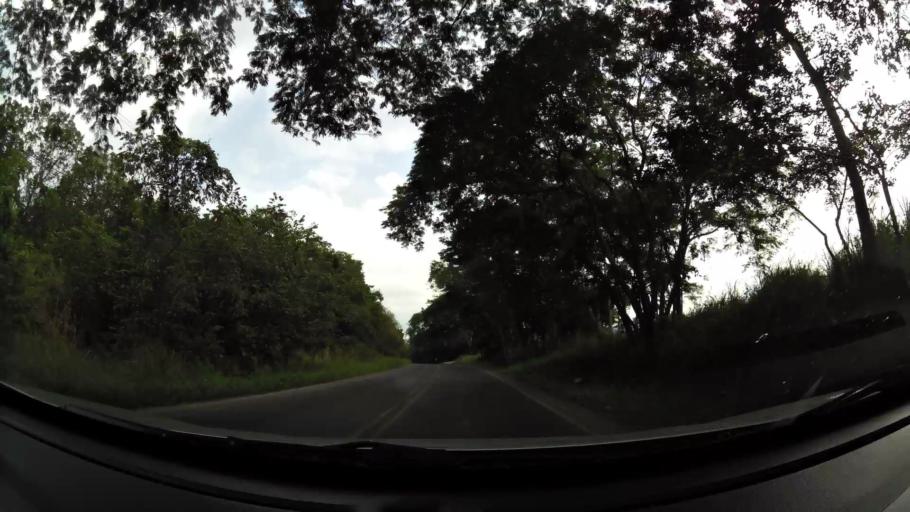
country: CR
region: Guanacaste
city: Juntas
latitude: 10.1997
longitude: -84.9573
